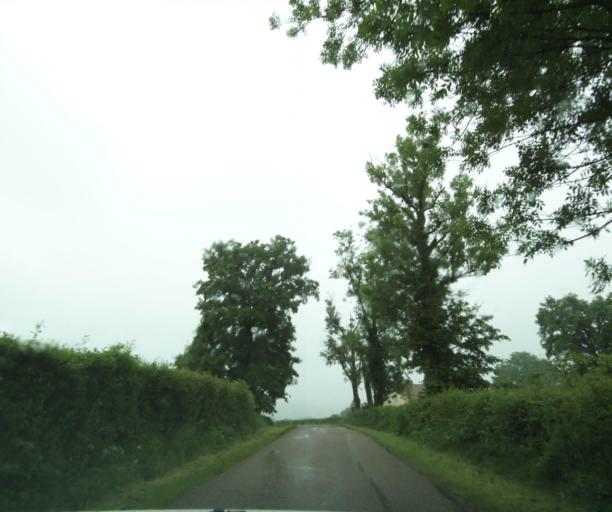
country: FR
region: Bourgogne
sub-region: Departement de Saone-et-Loire
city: Charolles
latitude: 46.3839
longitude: 4.2943
